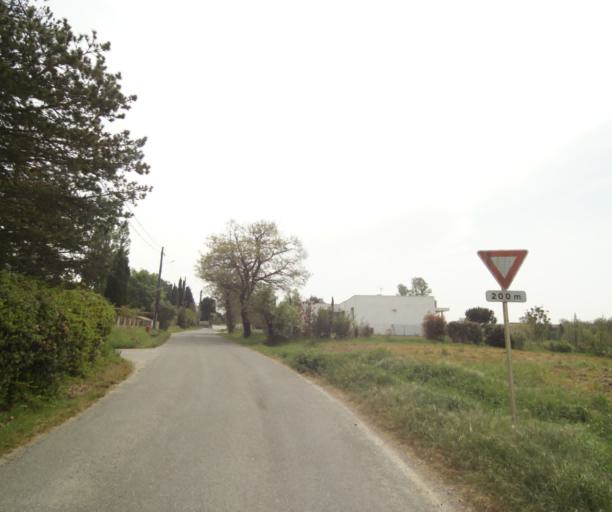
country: FR
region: Midi-Pyrenees
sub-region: Departement de la Haute-Garonne
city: Pechabou
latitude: 43.5002
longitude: 1.5027
